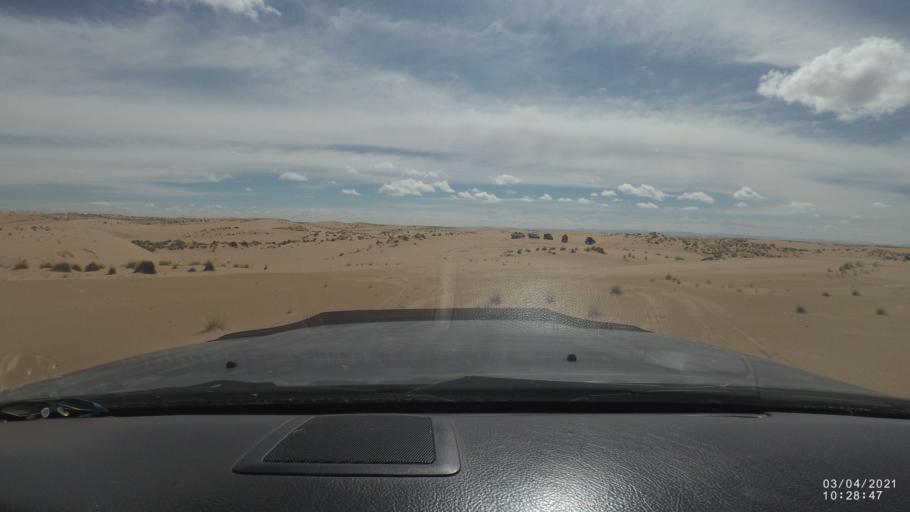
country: BO
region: Oruro
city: Poopo
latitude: -18.7060
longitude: -67.5226
